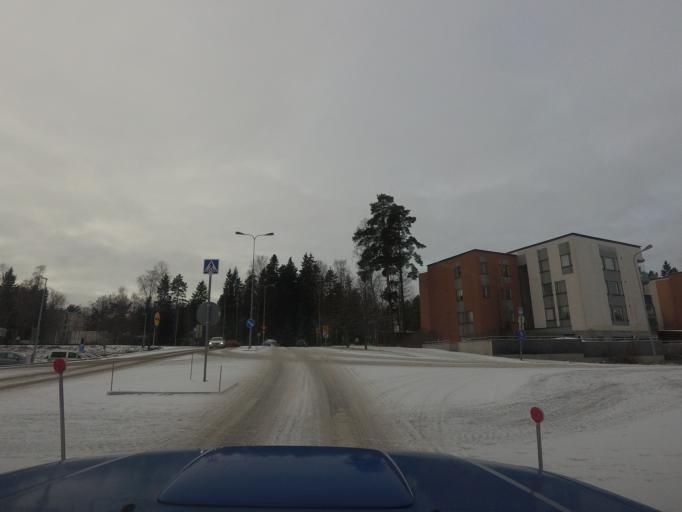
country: FI
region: Uusimaa
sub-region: Helsinki
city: Kilo
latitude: 60.2309
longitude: 24.7779
